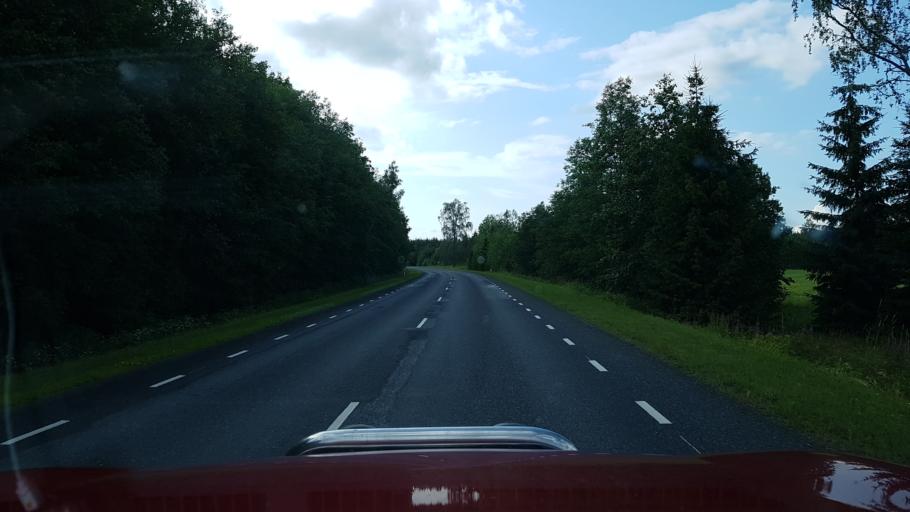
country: EE
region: Jaervamaa
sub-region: Jaerva-Jaani vald
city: Jarva-Jaani
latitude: 59.1021
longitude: 25.8145
